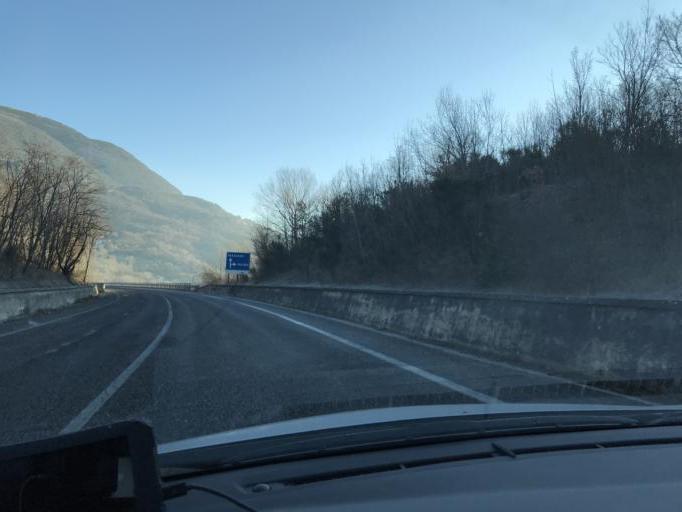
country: IT
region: Latium
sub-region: Provincia di Rieti
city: Fiamignano
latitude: 42.2611
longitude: 13.0975
